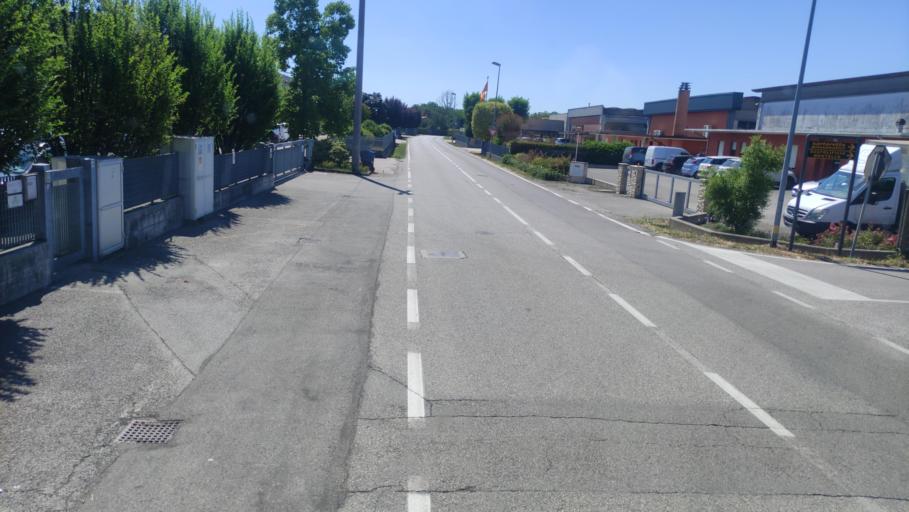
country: IT
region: Veneto
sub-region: Provincia di Treviso
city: Musano
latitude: 45.7384
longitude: 12.1204
